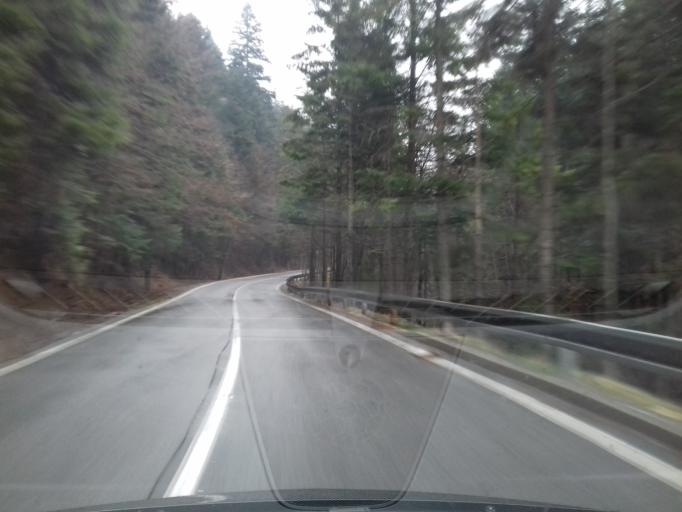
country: PL
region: Lesser Poland Voivodeship
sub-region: Powiat nowosadecki
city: Piwniczna-Zdroj
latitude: 49.3911
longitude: 20.6987
